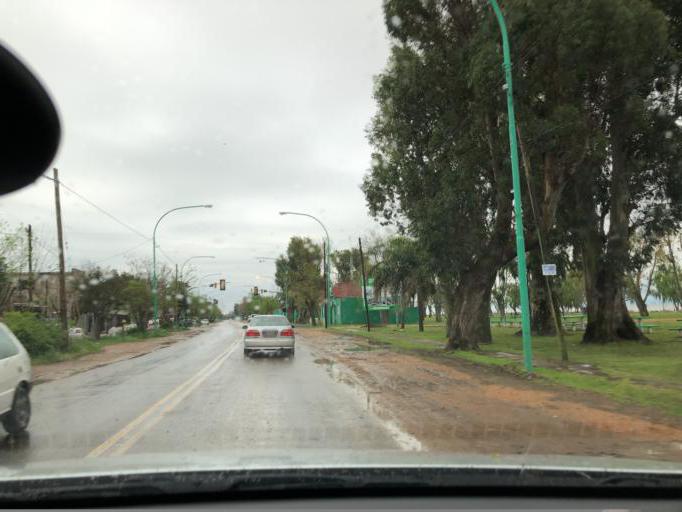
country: AR
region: Buenos Aires
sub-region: Partido de Ensenada
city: Ensenada
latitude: -34.8281
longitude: -57.9573
